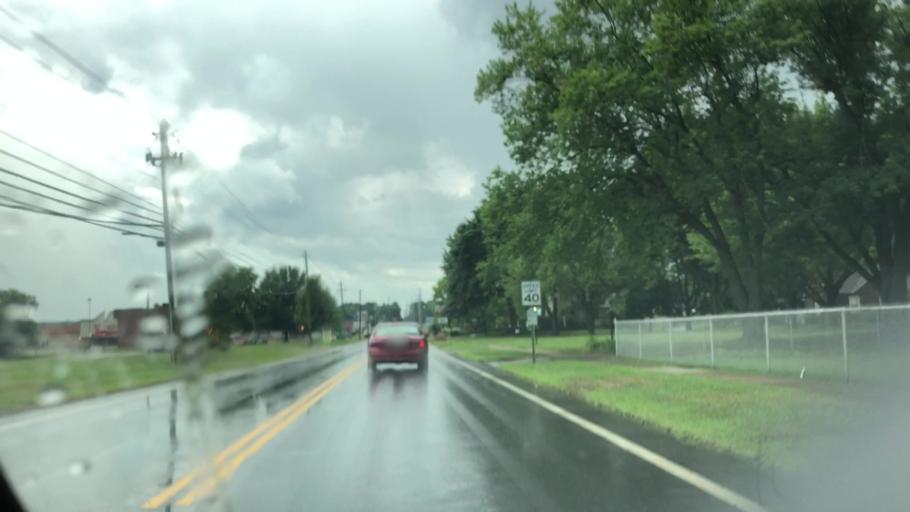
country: US
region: Ohio
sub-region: Stark County
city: Massillon
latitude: 40.8259
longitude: -81.5028
